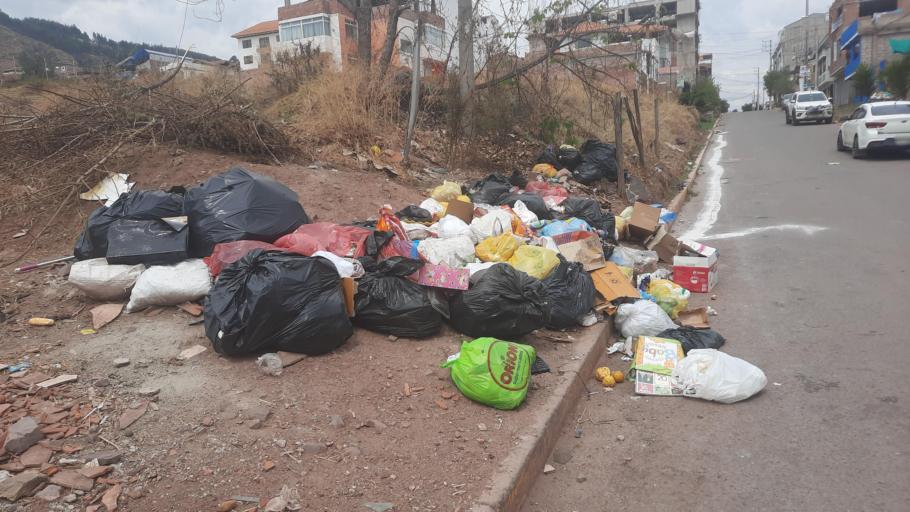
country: PE
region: Cusco
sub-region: Provincia de Cusco
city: Saylla
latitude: -13.5284
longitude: -71.9015
